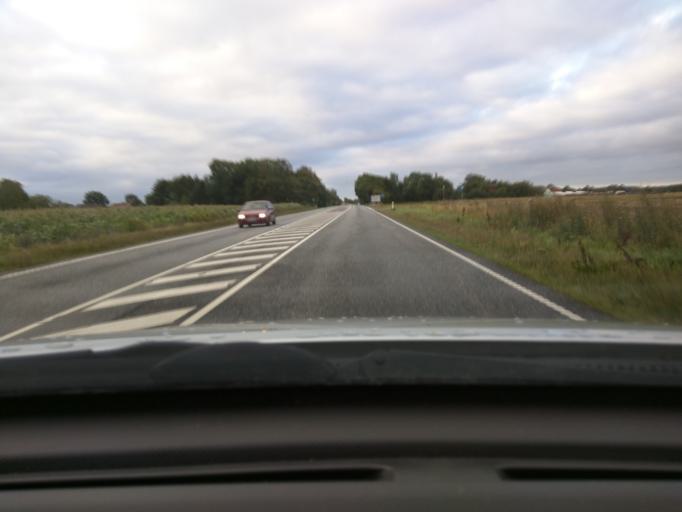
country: DK
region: Central Jutland
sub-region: Silkeborg Kommune
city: Kjellerup
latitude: 56.2905
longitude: 9.3211
